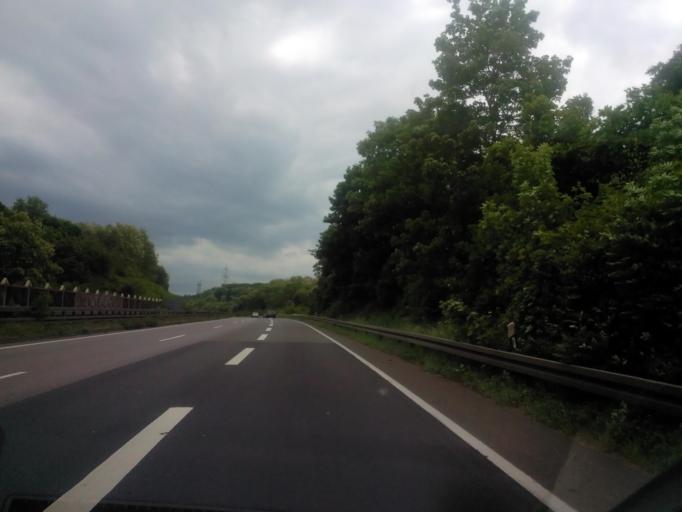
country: DE
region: Saarland
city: Saarlouis
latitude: 49.2938
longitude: 6.7539
